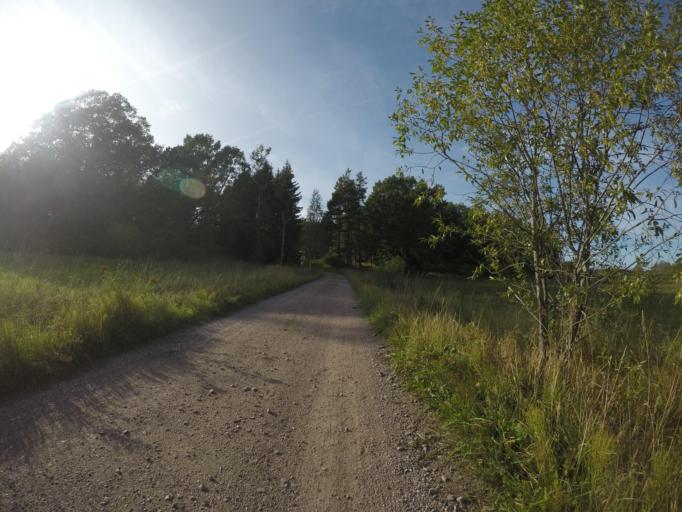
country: SE
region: Soedermanland
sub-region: Eskilstuna Kommun
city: Kvicksund
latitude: 59.4837
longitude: 16.2894
